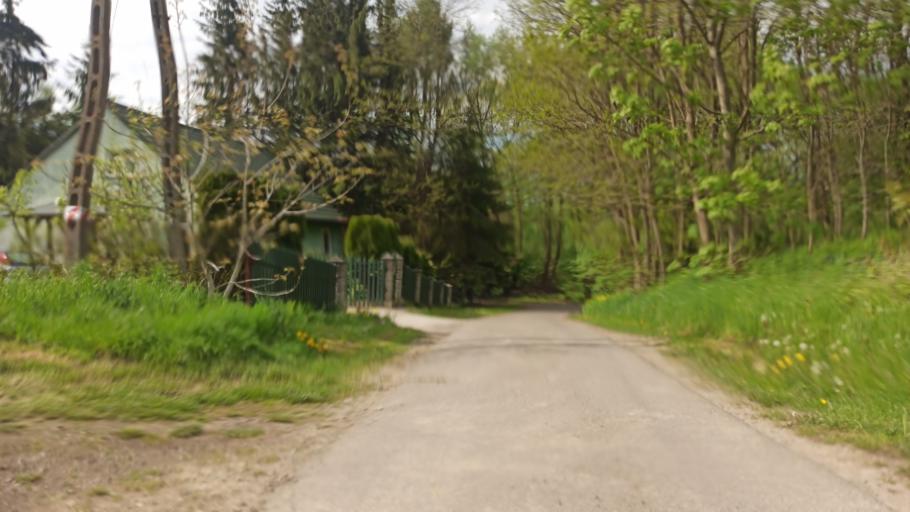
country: PL
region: Subcarpathian Voivodeship
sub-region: Powiat jaroslawski
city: Radymno
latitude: 49.9386
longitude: 22.8194
